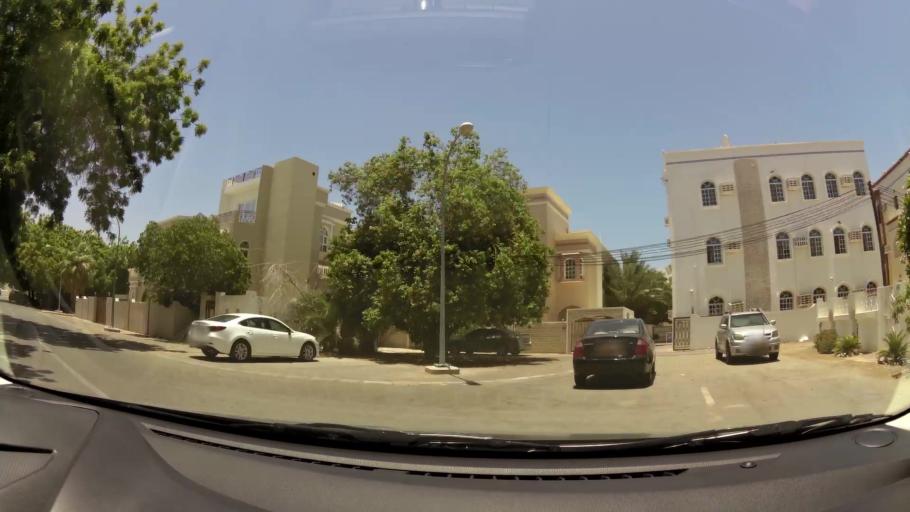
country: OM
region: Muhafazat Masqat
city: Bawshar
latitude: 23.5965
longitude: 58.3930
